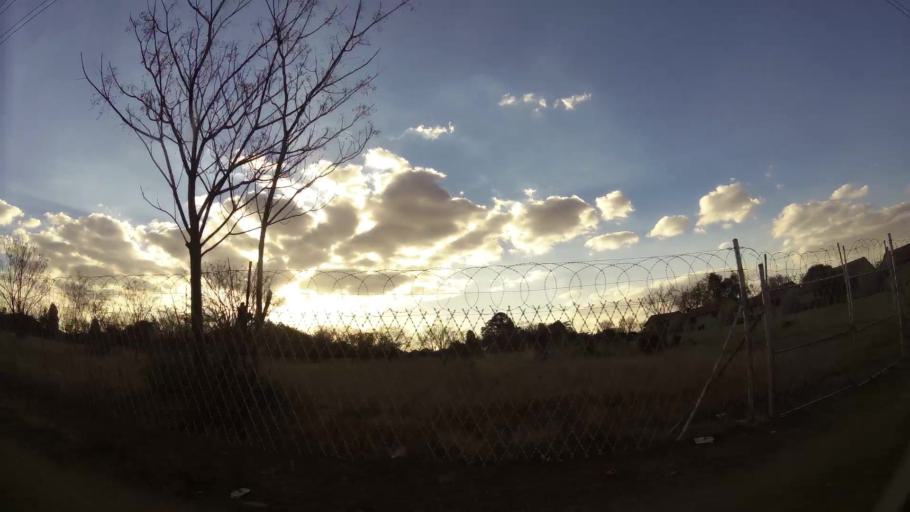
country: ZA
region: Gauteng
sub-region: City of Johannesburg Metropolitan Municipality
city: Diepsloot
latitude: -25.9958
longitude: 27.9970
